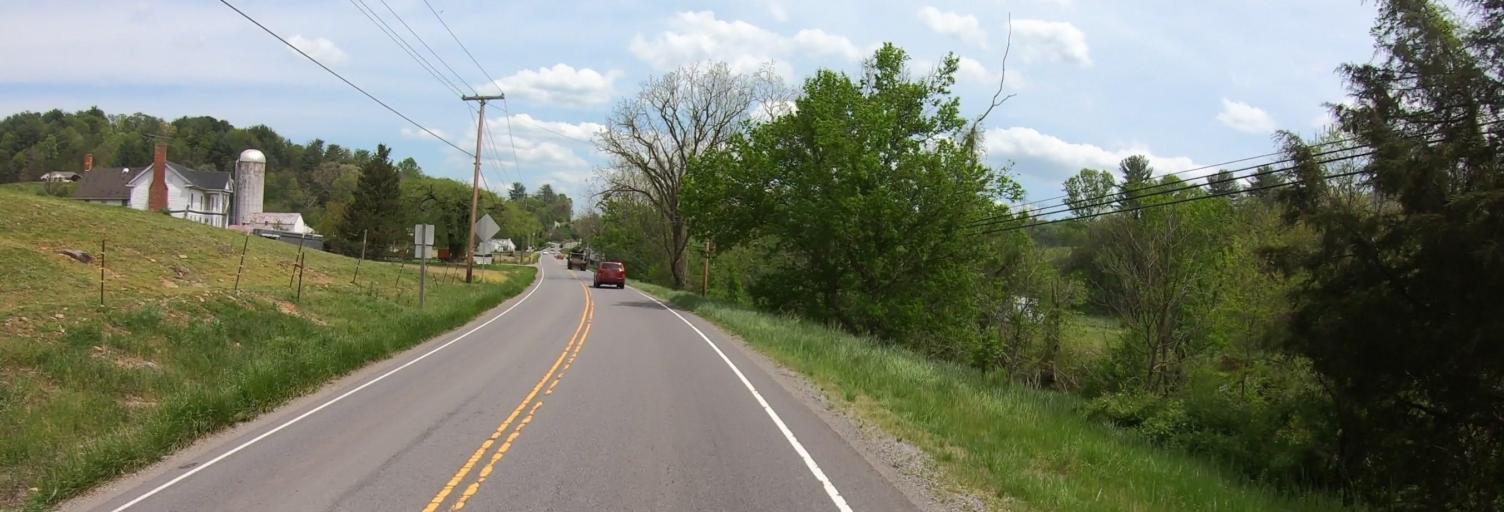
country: US
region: Virginia
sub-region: Roanoke County
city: Cave Spring
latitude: 37.1986
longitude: -80.0511
